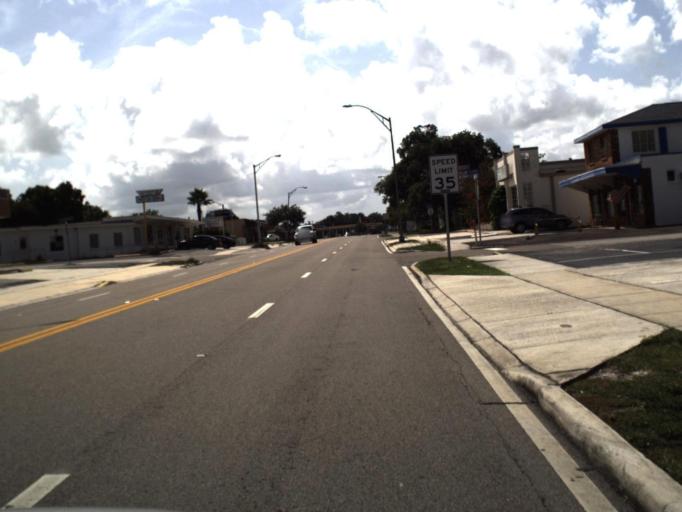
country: US
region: Florida
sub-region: Pinellas County
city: Clearwater
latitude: 27.9635
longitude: -82.7780
